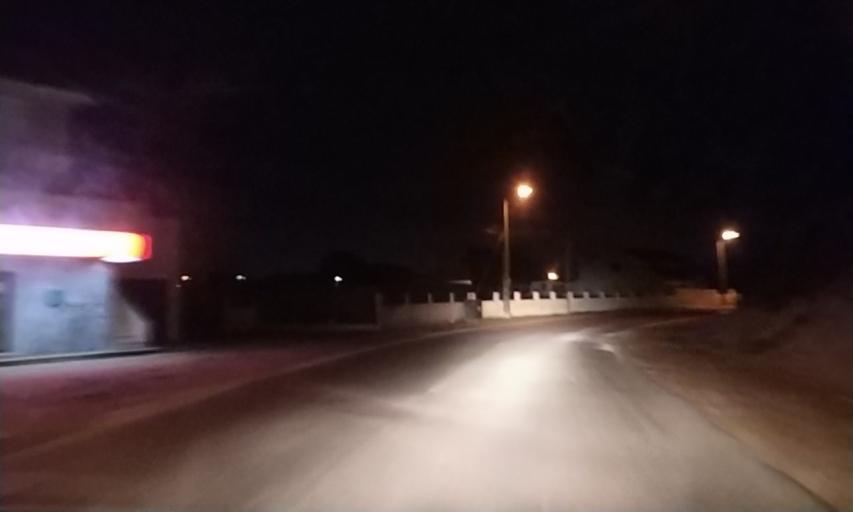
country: PT
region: Setubal
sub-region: Setubal
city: Setubal
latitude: 38.5223
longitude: -8.8284
